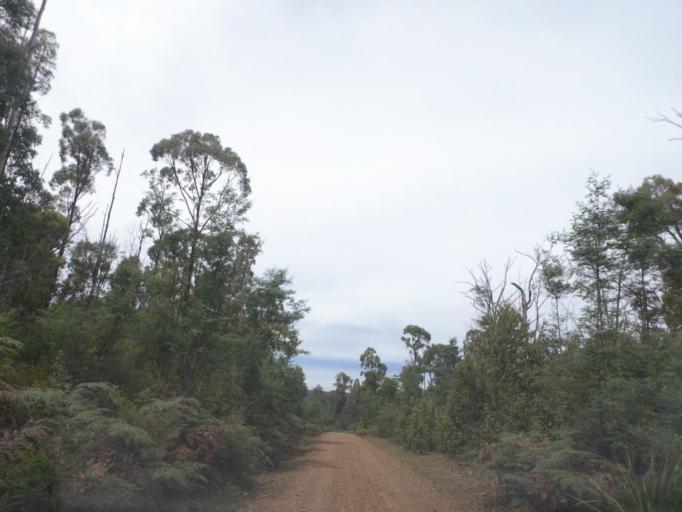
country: AU
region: Victoria
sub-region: Yarra Ranges
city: Healesville
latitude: -37.4392
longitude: 145.5812
